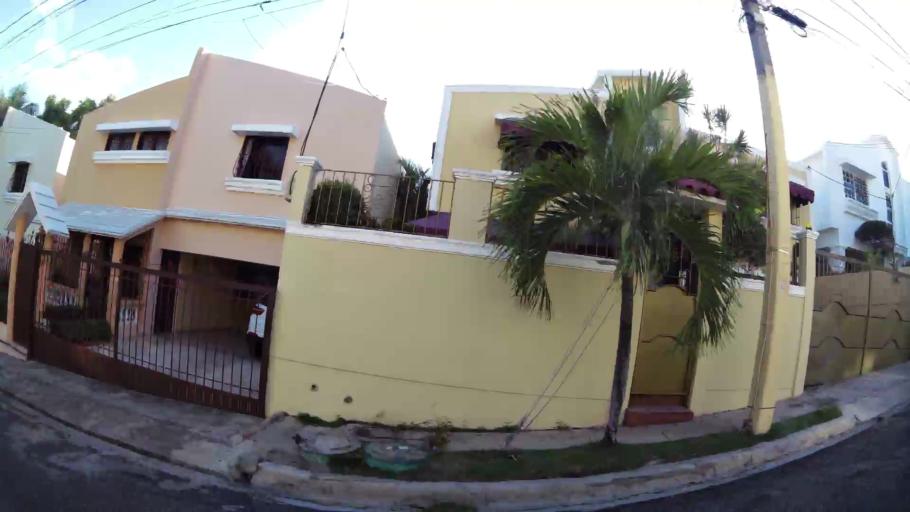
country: DO
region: Nacional
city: Santo Domingo
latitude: 18.4931
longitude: -69.9683
